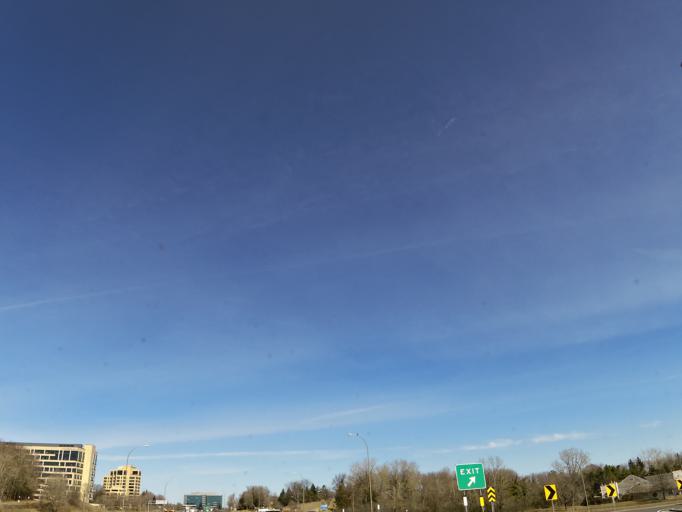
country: US
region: Minnesota
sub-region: Hennepin County
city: Edina
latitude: 44.8913
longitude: -93.3992
